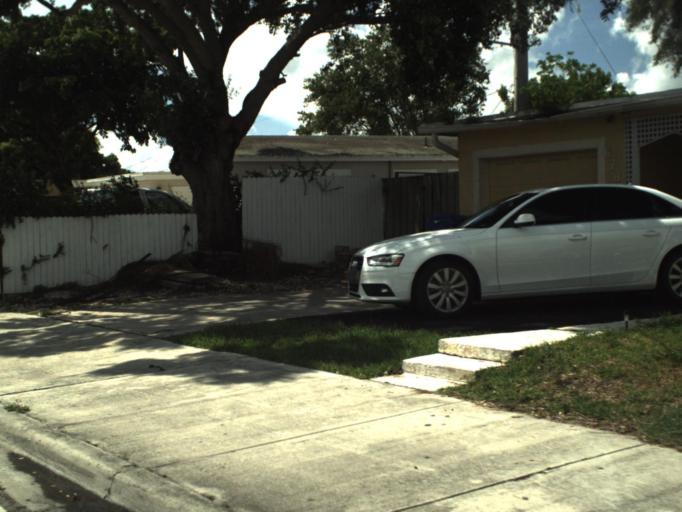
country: US
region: Florida
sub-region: Broward County
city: Pembroke Pines
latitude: 26.0318
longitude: -80.2241
